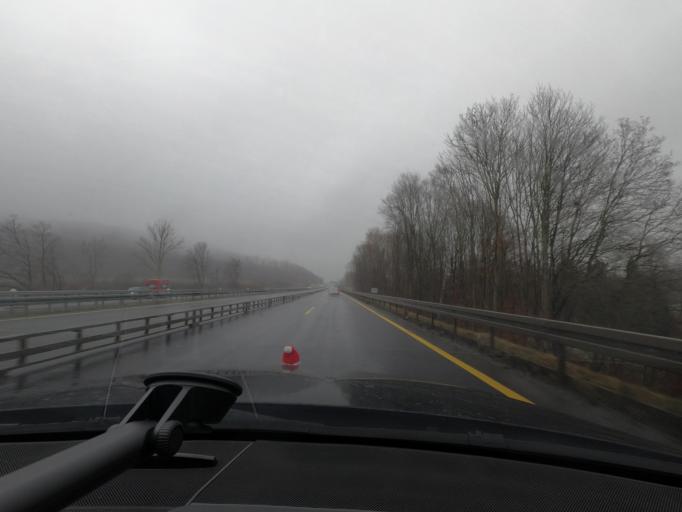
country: DE
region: Lower Saxony
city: Seesen
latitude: 51.8652
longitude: 10.1266
